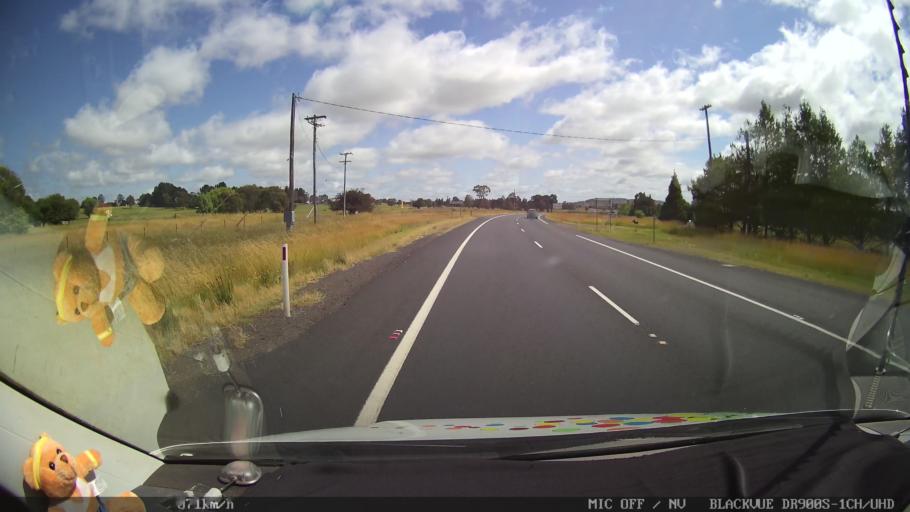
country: AU
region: New South Wales
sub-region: Glen Innes Severn
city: Glen Innes
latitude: -29.9215
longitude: 151.7249
